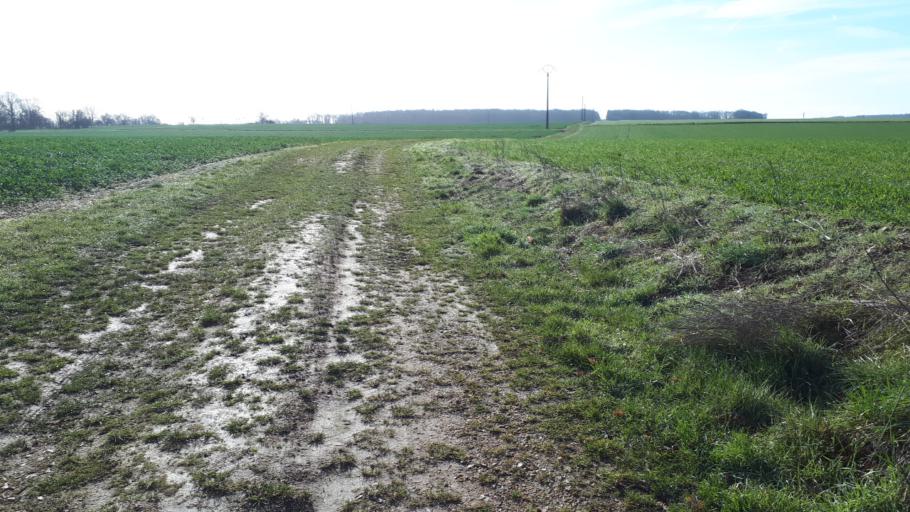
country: FR
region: Centre
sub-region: Departement du Loir-et-Cher
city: Villiers-sur-Loir
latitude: 47.8030
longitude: 0.9726
